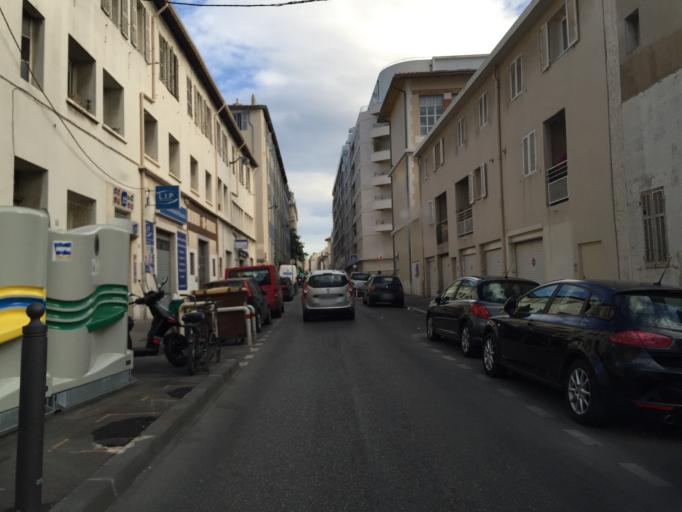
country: FR
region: Provence-Alpes-Cote d'Azur
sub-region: Departement des Bouches-du-Rhone
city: Marseille 02
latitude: 43.3024
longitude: 5.3674
